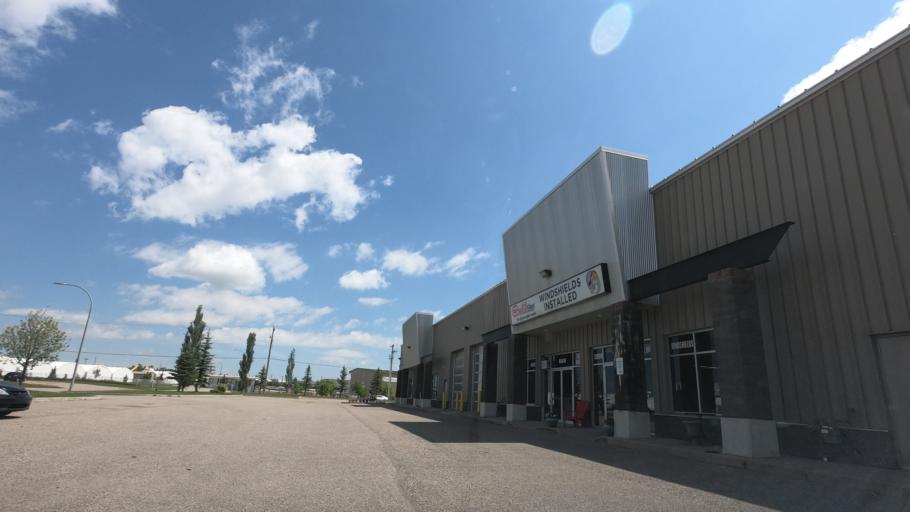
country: CA
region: Alberta
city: Airdrie
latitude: 51.2953
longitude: -113.9968
